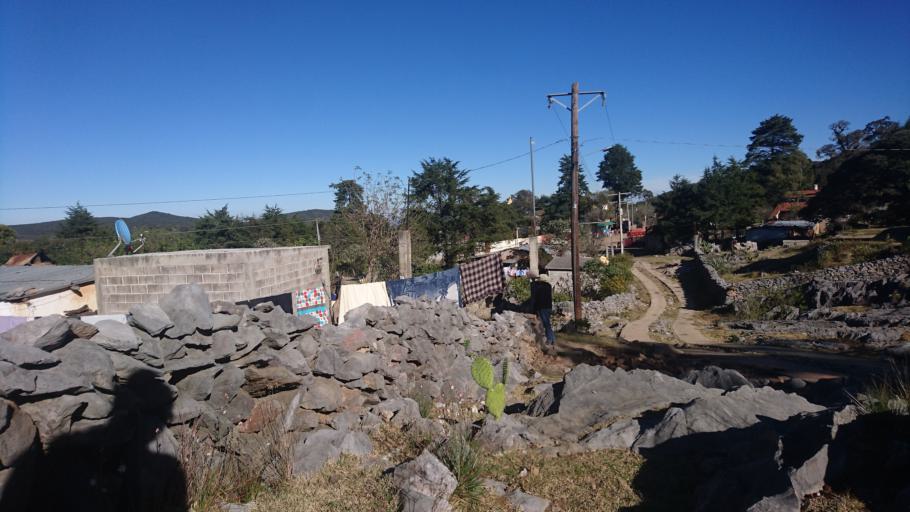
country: MX
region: San Luis Potosi
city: Zaragoza
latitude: 22.0200
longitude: -100.6027
